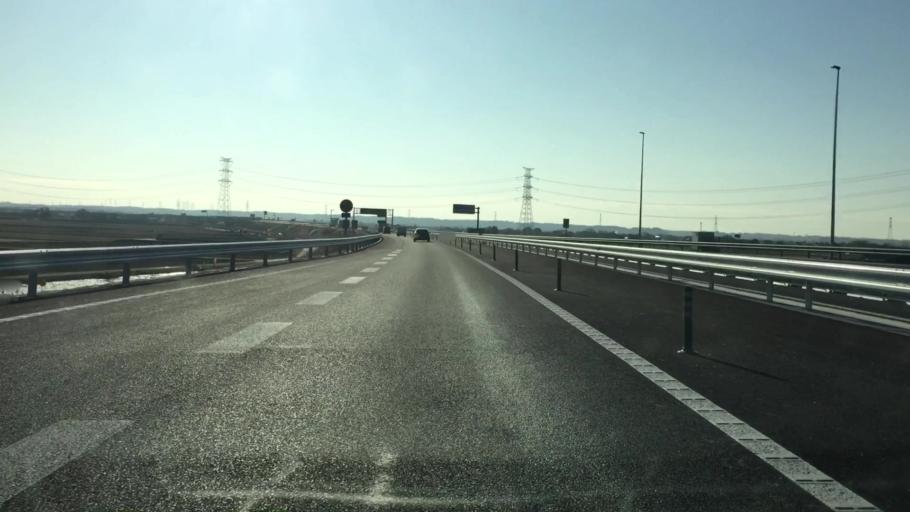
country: JP
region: Ibaraki
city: Inashiki
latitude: 35.9230
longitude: 140.3482
